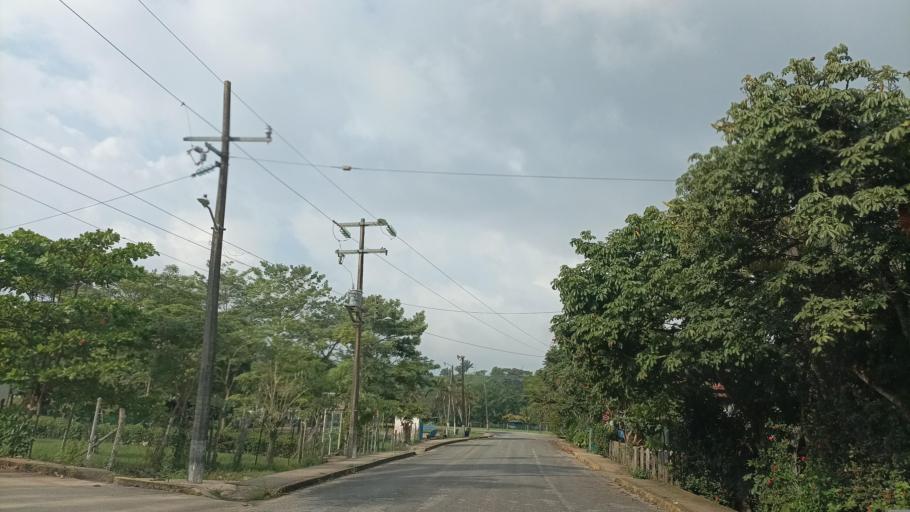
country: MX
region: Veracruz
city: Allende
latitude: 18.1254
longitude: -94.2828
